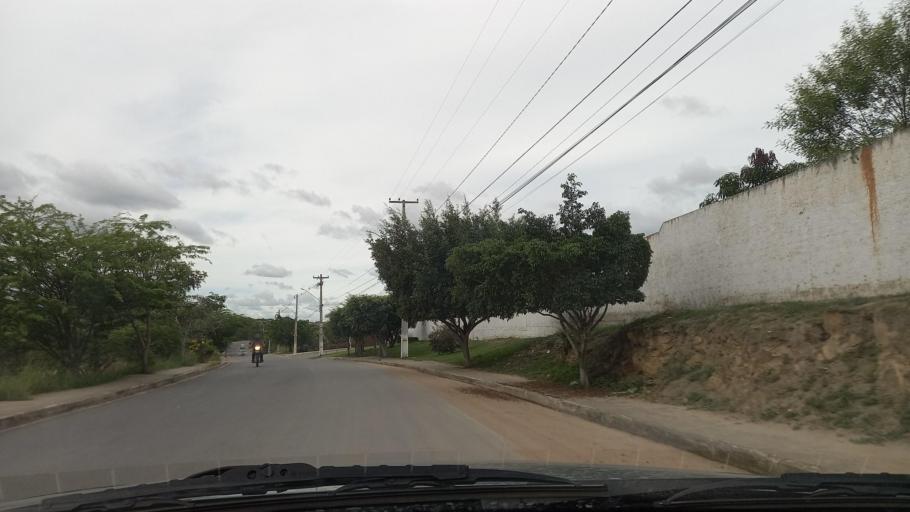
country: BR
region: Pernambuco
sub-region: Gravata
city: Gravata
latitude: -8.2117
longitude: -35.5994
